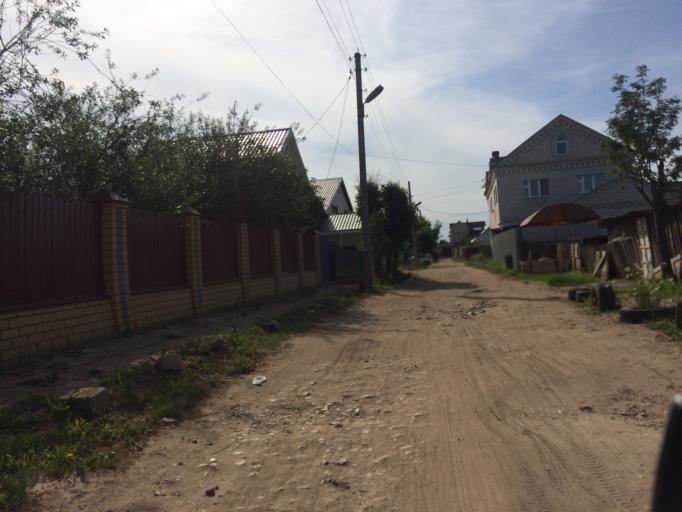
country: RU
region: Mariy-El
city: Yoshkar-Ola
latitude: 56.6522
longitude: 47.9162
